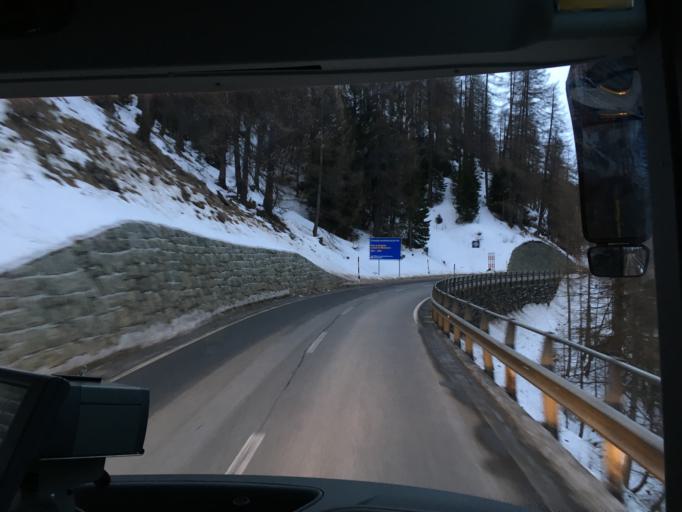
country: CH
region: Grisons
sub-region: Maloja District
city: Silvaplana
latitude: 46.5015
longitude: 9.6409
